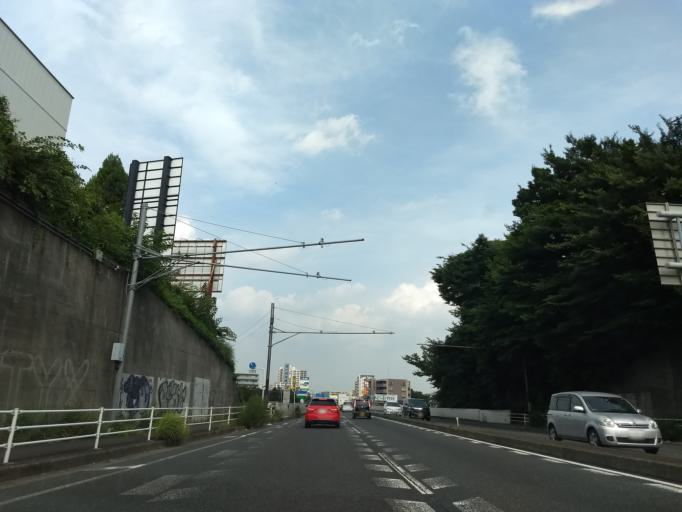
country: JP
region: Tokyo
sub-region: Machida-shi
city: Machida
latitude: 35.5141
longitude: 139.4609
